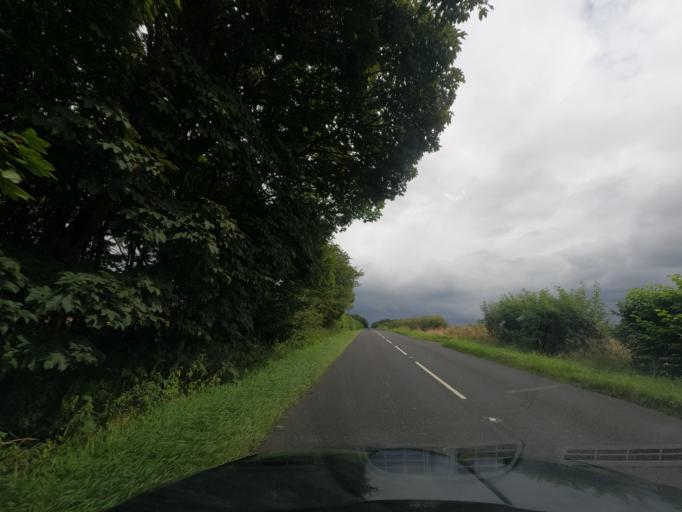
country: GB
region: England
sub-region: Northumberland
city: Ancroft
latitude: 55.7185
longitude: -1.9882
